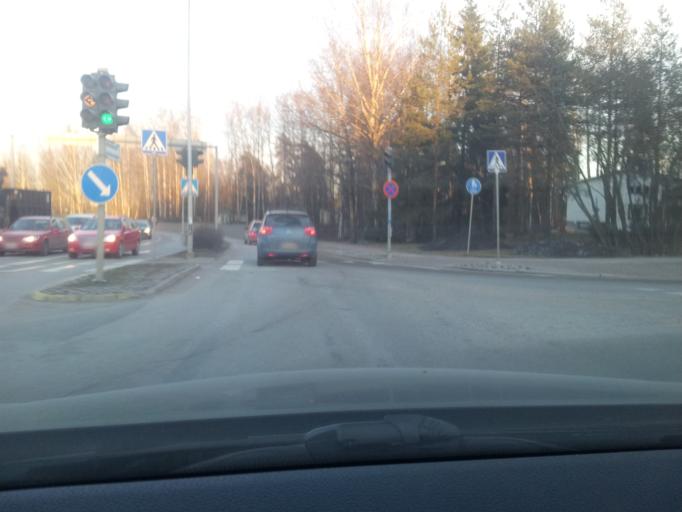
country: FI
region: Uusimaa
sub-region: Helsinki
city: Otaniemi
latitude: 60.1827
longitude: 24.7948
